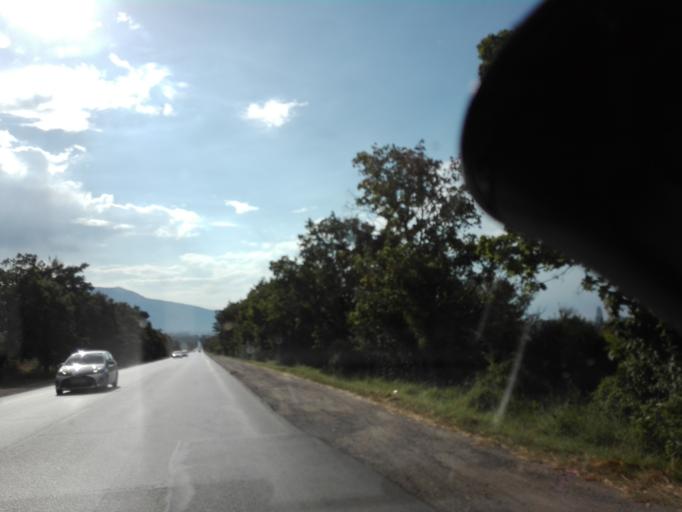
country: BG
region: Sofia-Capital
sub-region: Stolichna Obshtina
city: Sofia
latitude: 42.6214
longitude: 23.4342
